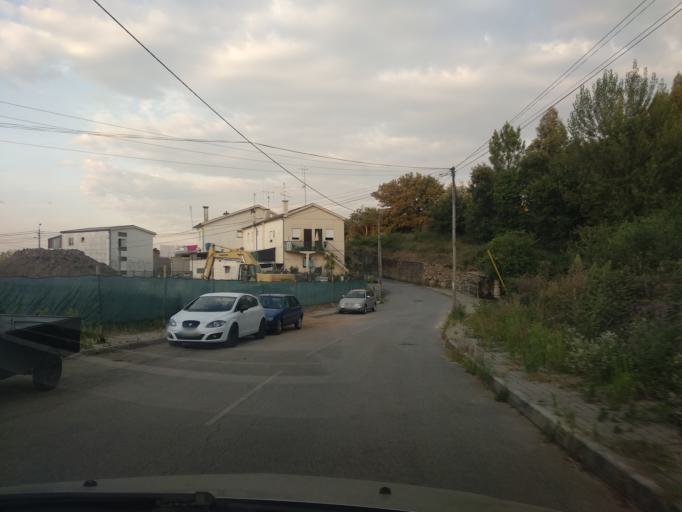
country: PT
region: Braga
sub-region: Braga
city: Braga
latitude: 41.5295
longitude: -8.4497
